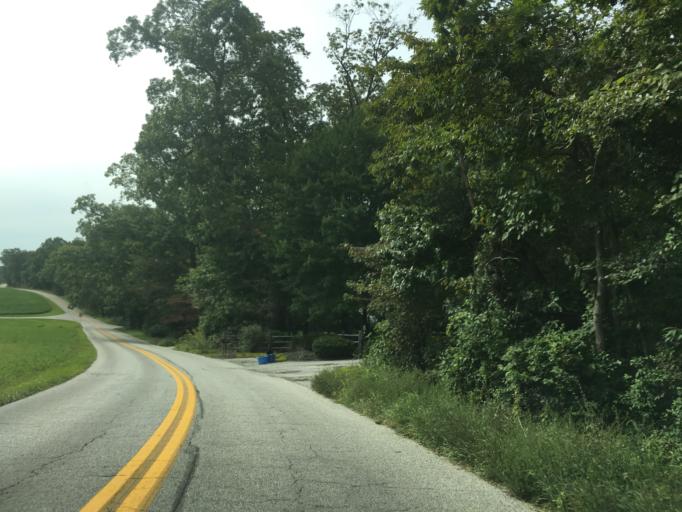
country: US
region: Maryland
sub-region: Baltimore County
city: Hunt Valley
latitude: 39.5656
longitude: -76.6776
